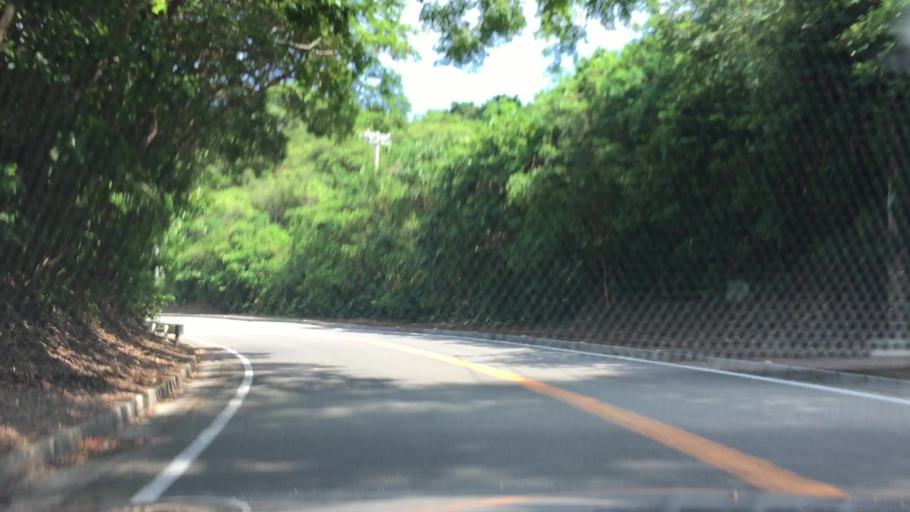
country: JP
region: Okinawa
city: Ishigaki
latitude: 24.5124
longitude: 124.2656
